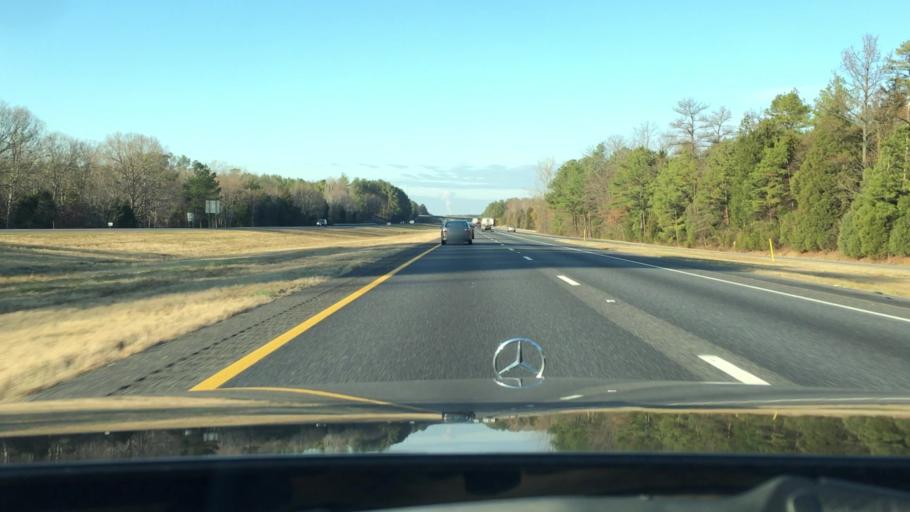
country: US
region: South Carolina
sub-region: York County
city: Lesslie
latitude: 34.7652
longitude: -81.0370
